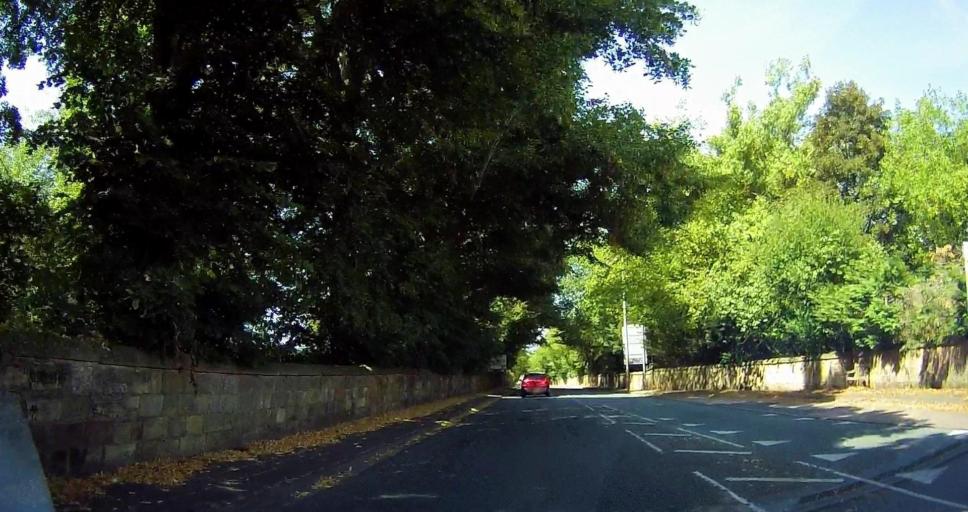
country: GB
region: England
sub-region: Staffordshire
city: Codsall
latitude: 52.6065
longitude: -2.1942
